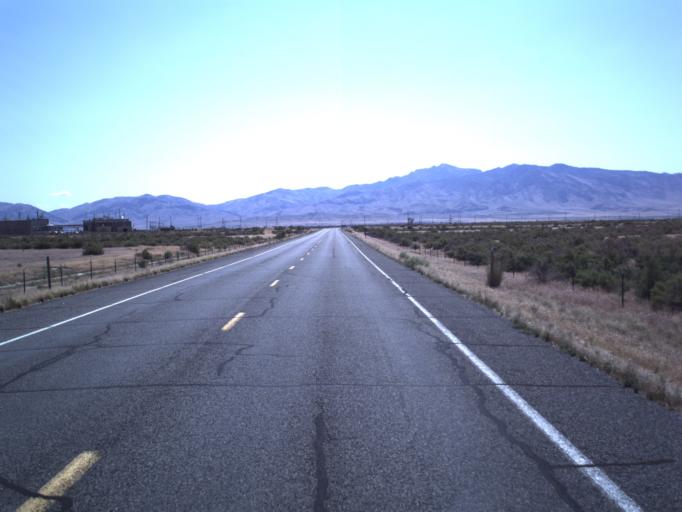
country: US
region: Utah
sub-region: Millard County
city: Delta
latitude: 39.4676
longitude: -112.4478
